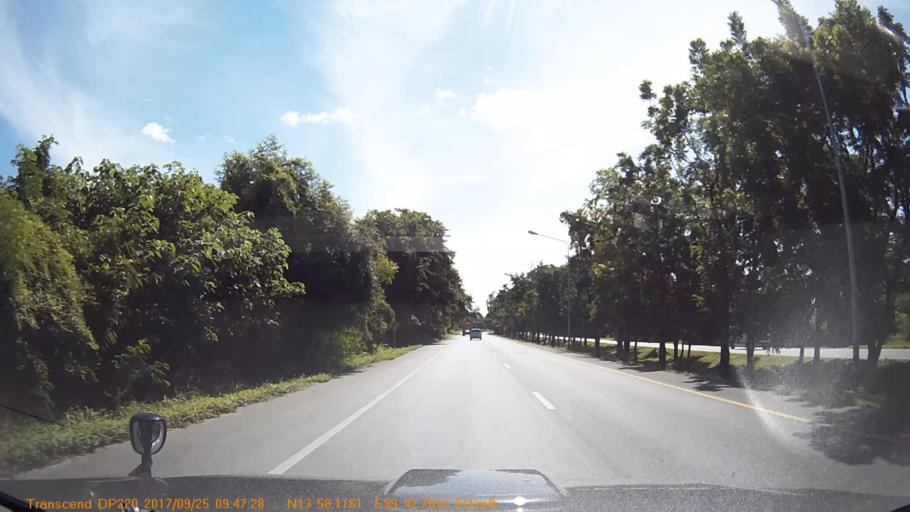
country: TH
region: Kanchanaburi
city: Tha Maka
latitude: 13.9686
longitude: 99.7131
